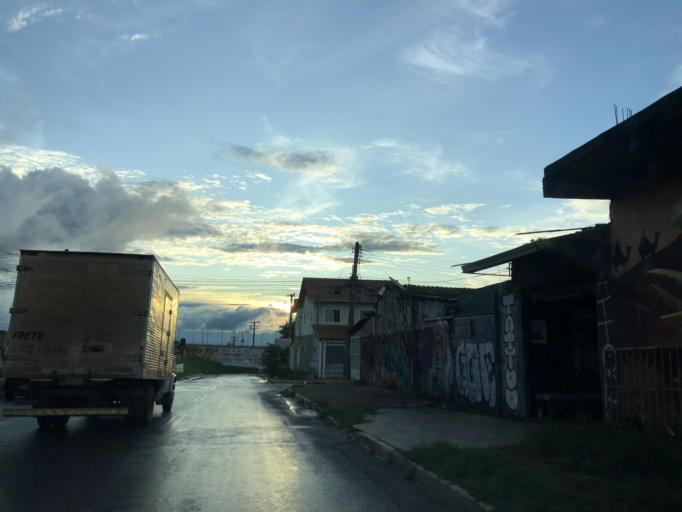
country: BR
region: Federal District
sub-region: Brasilia
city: Brasilia
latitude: -15.8331
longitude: -48.1048
